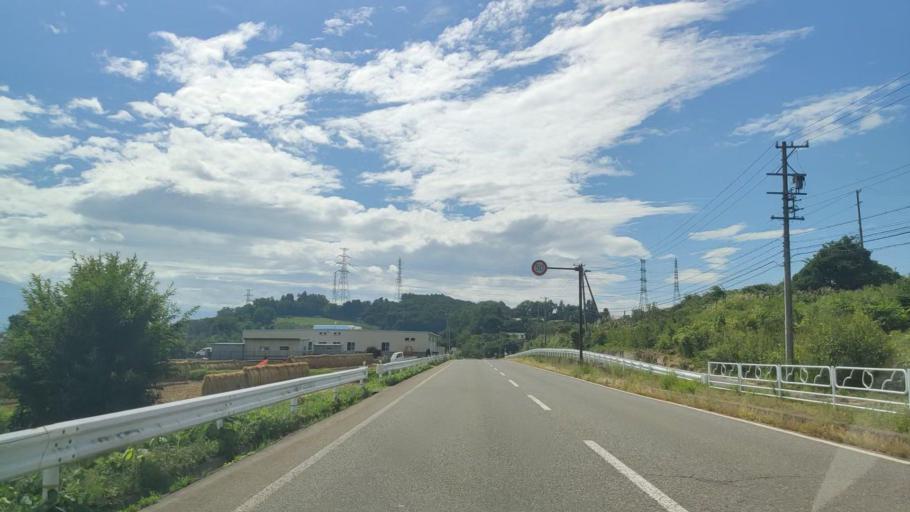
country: JP
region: Nagano
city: Nakano
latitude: 36.7400
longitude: 138.3055
